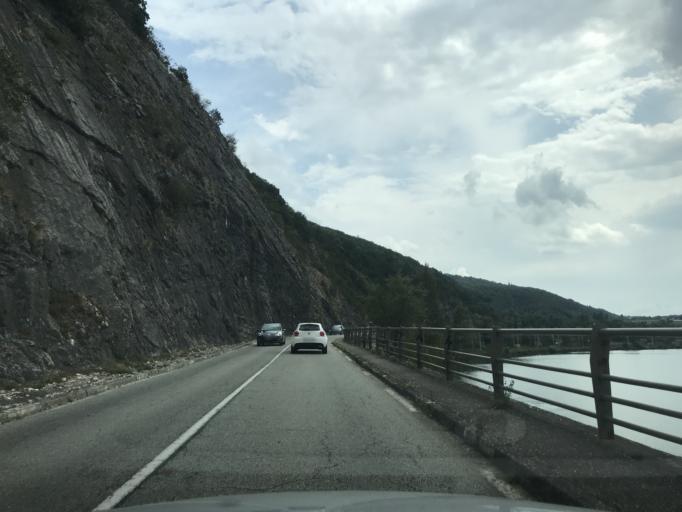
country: FR
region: Rhone-Alpes
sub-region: Departement de la Savoie
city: Brison-Saint-Innocent
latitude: 45.7406
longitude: 5.8908
